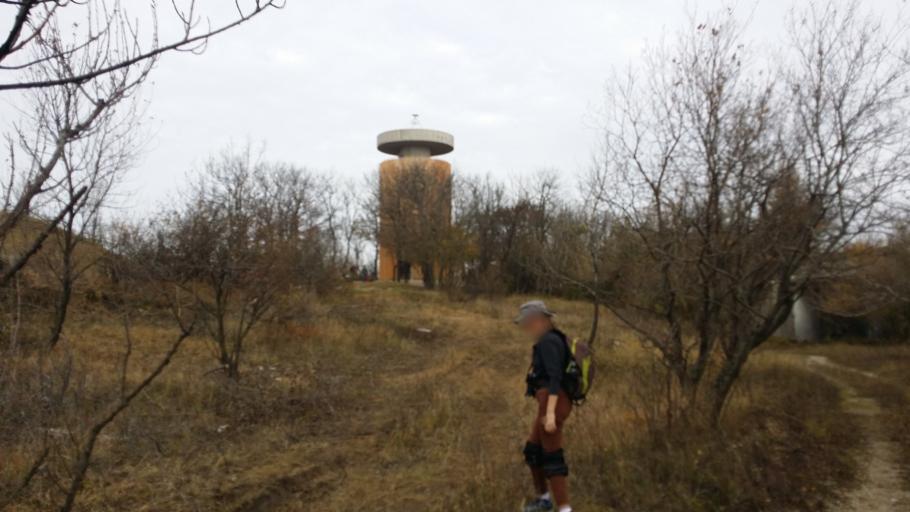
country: HU
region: Pest
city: Pilisszanto
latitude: 47.6880
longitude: 18.8730
